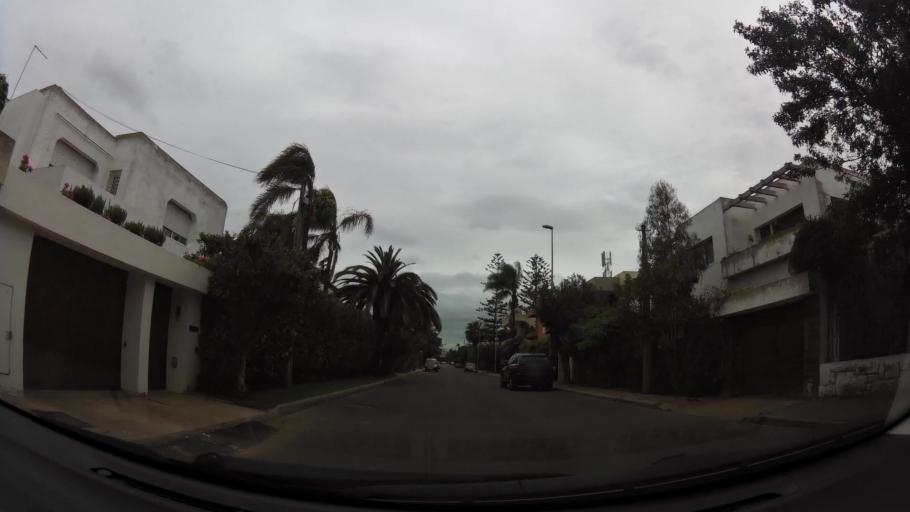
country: MA
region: Grand Casablanca
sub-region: Casablanca
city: Casablanca
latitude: 33.5834
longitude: -7.6569
